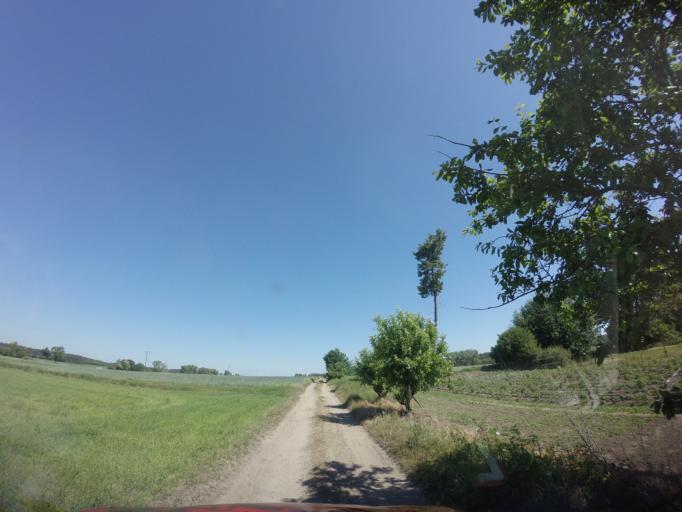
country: PL
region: West Pomeranian Voivodeship
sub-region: Powiat choszczenski
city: Choszczno
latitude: 53.2297
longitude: 15.3865
